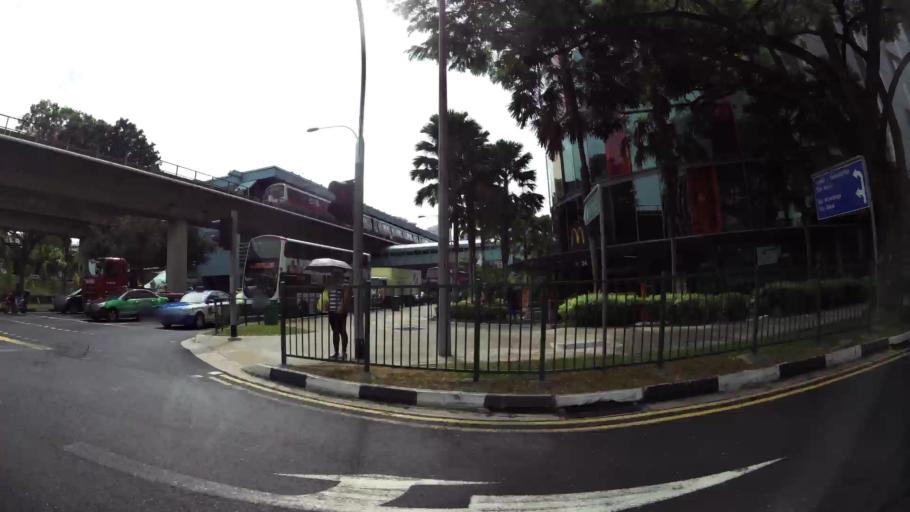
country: SG
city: Singapore
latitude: 1.3158
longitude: 103.7645
